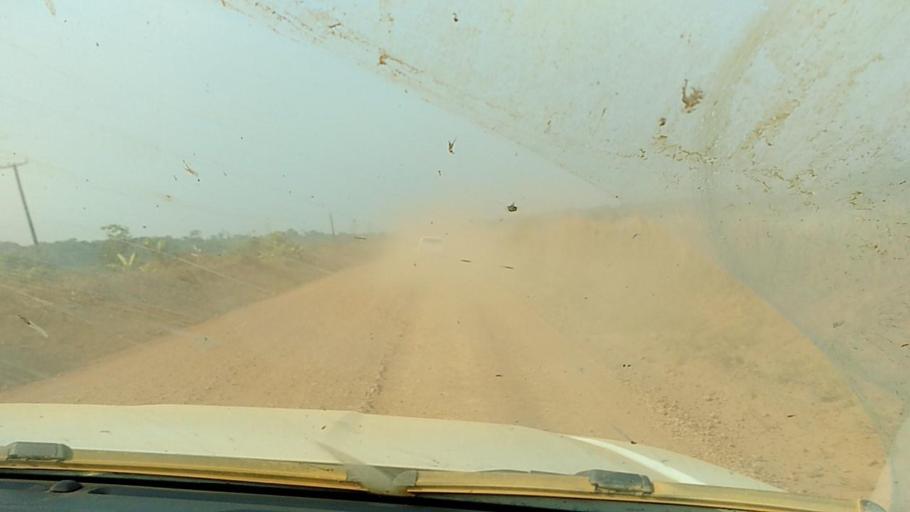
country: BR
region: Rondonia
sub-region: Porto Velho
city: Porto Velho
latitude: -8.7658
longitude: -64.0710
